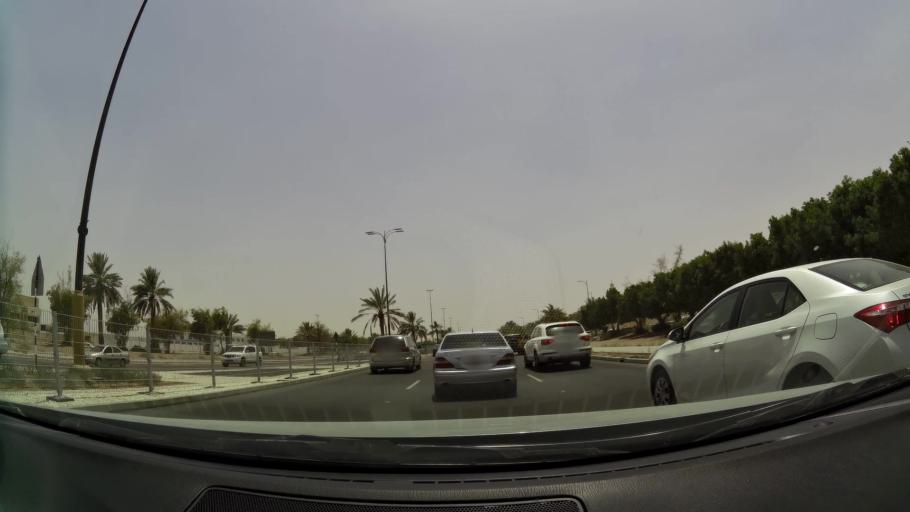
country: AE
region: Abu Dhabi
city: Al Ain
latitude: 24.2001
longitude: 55.7139
